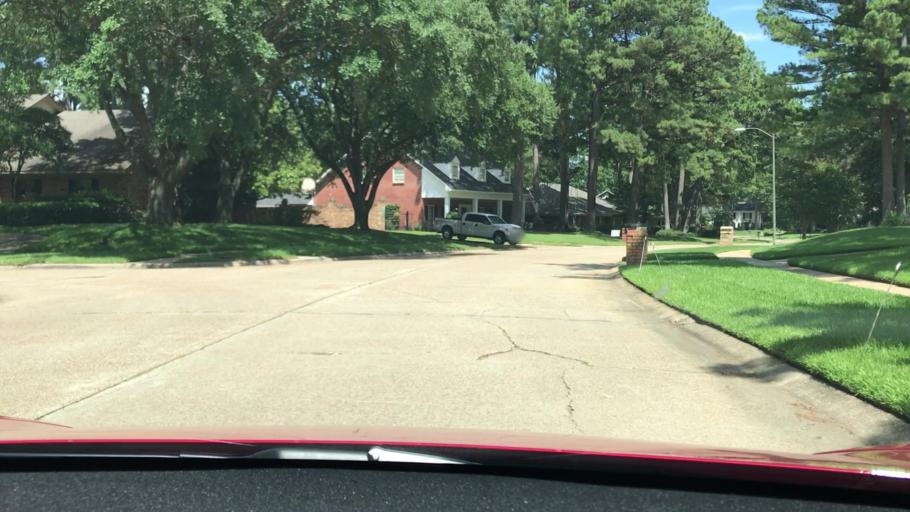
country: US
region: Louisiana
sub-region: Bossier Parish
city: Bossier City
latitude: 32.4233
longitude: -93.7325
